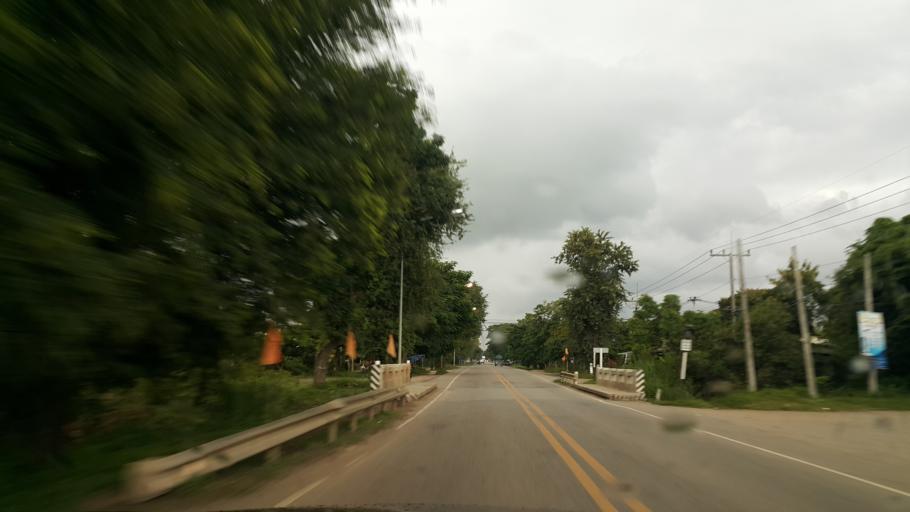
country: TH
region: Phayao
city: Phu Kam Yao
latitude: 19.2380
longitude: 100.0485
